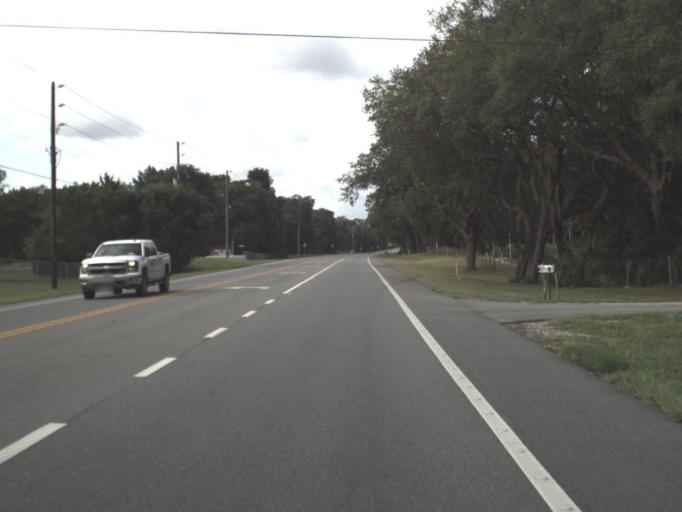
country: US
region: Florida
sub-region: Hernando County
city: Ridge Manor
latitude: 28.4879
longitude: -82.1752
